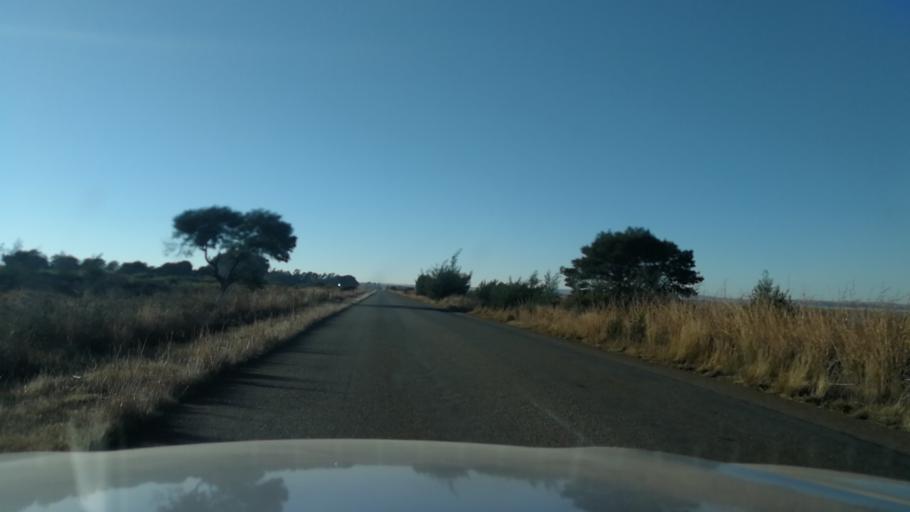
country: ZA
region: North-West
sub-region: Bojanala Platinum District Municipality
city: Rustenburg
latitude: -25.9545
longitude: 27.1891
